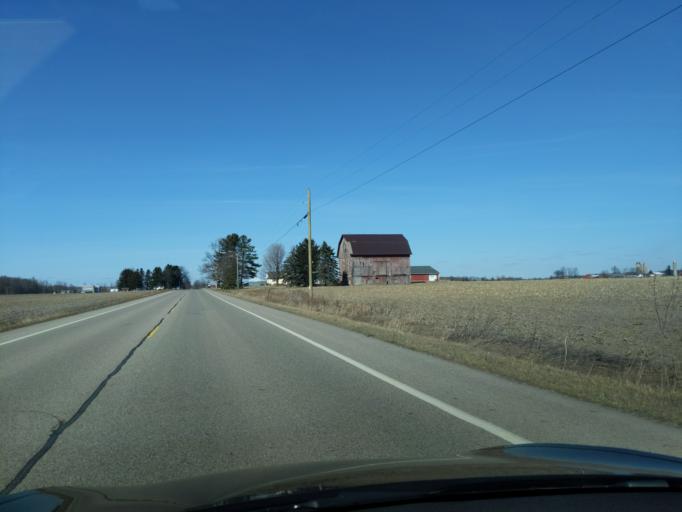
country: US
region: Michigan
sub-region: Ionia County
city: Lake Odessa
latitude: 42.8222
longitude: -85.1337
